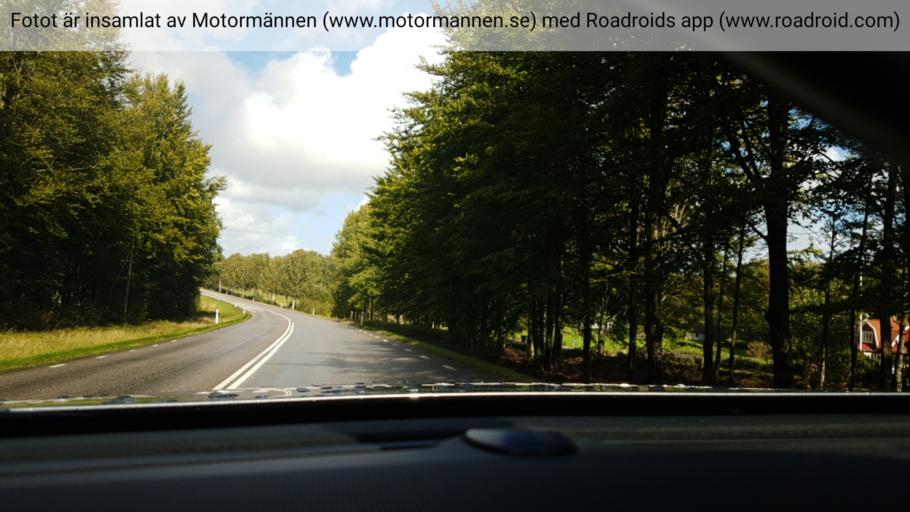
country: SE
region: Vaestra Goetaland
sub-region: Alingsas Kommun
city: Sollebrunn
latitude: 58.0679
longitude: 12.4798
